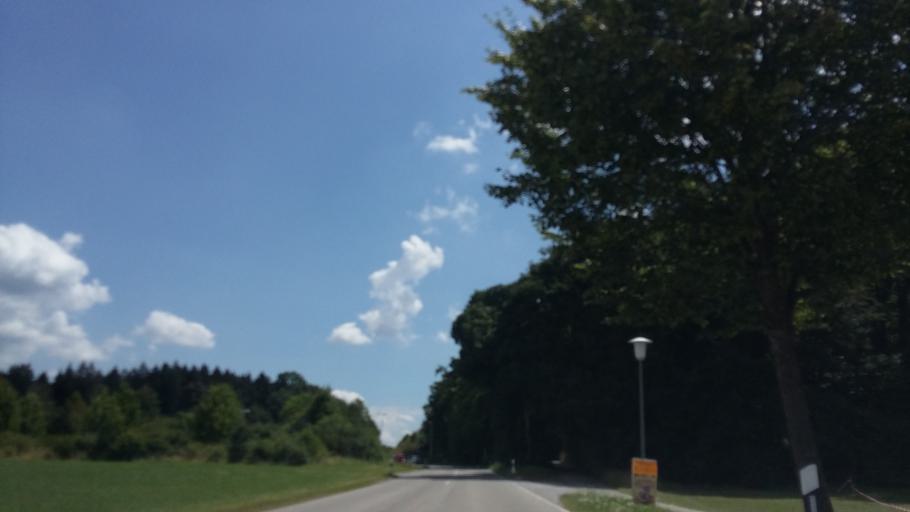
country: DE
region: Bavaria
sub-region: Upper Bavaria
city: Starnberg
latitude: 48.0192
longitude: 11.3258
